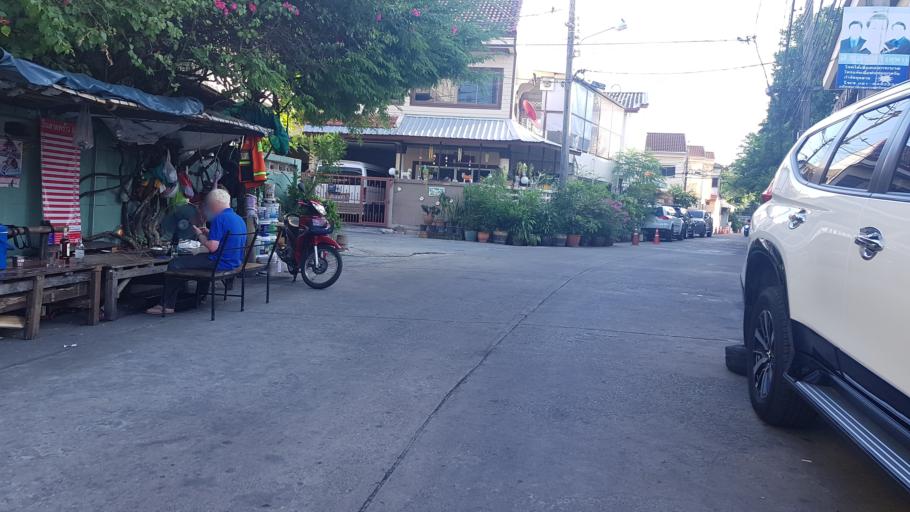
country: TH
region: Bangkok
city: Wang Thonglang
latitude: 13.7817
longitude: 100.6263
